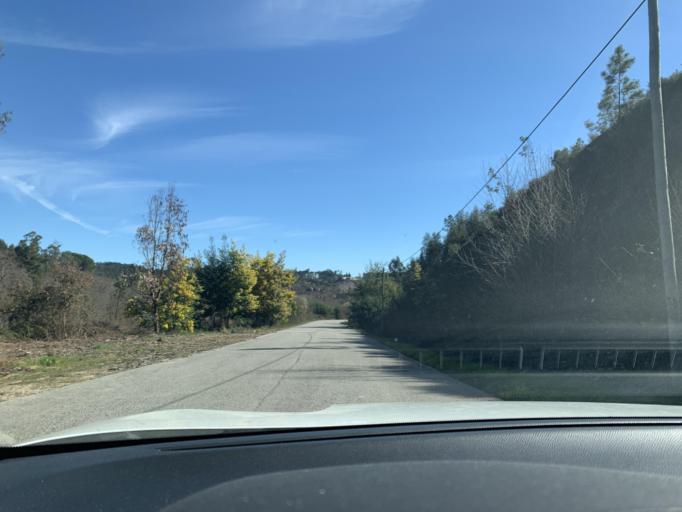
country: PT
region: Viseu
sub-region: Concelho de Tondela
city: Tondela
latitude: 40.6020
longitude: -8.0296
